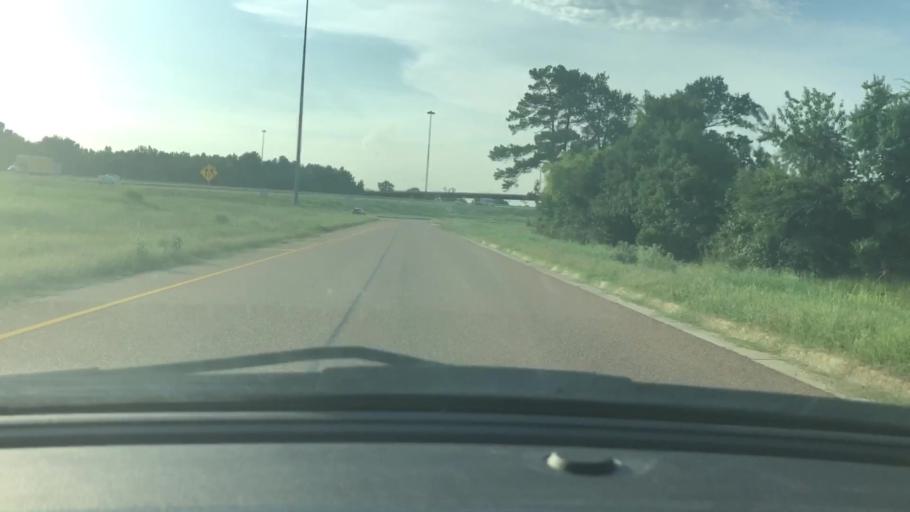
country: US
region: Texas
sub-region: Bowie County
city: Wake Village
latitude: 33.3893
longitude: -94.0954
